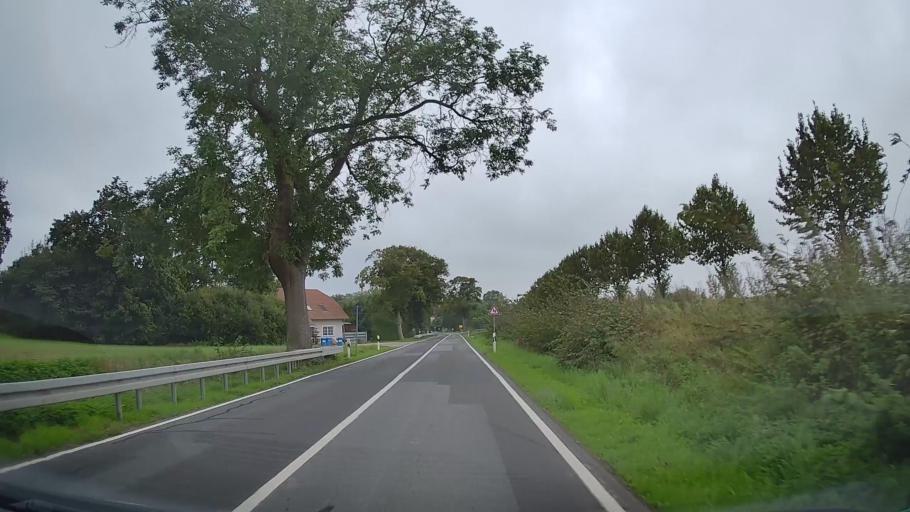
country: DE
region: Mecklenburg-Vorpommern
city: Schwaan
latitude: 53.9170
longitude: 12.1925
